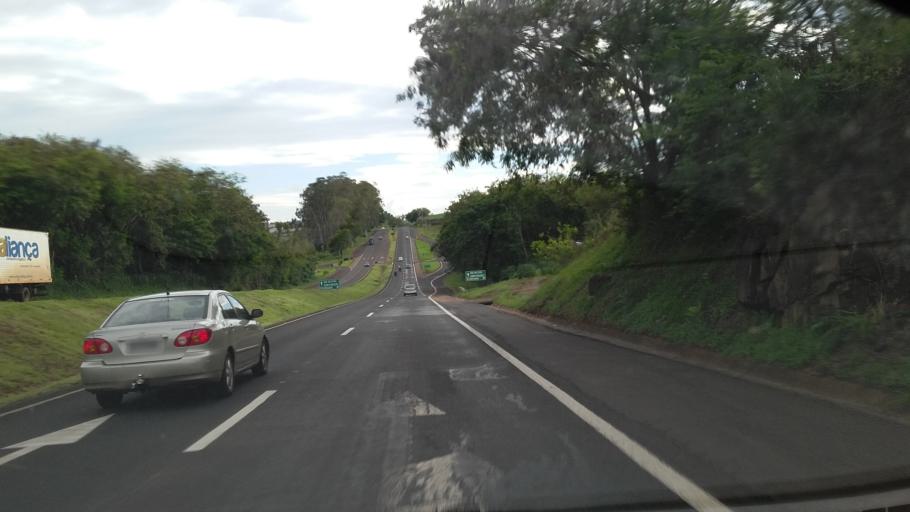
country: BR
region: Parana
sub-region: Paicandu
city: Paicandu
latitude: -23.5188
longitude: -52.0285
